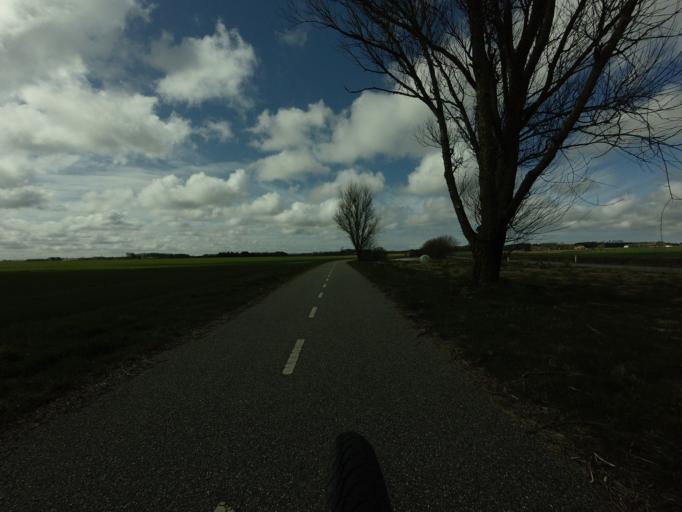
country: DK
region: North Denmark
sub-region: Hjorring Kommune
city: Vra
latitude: 57.3532
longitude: 9.8998
